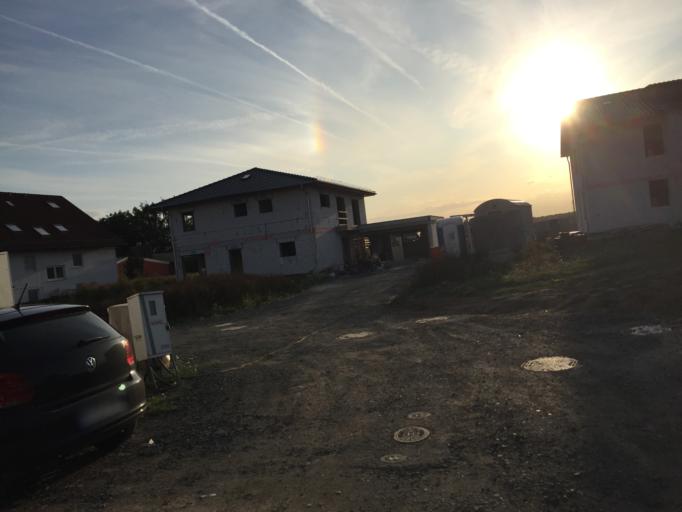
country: DE
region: Hesse
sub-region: Regierungsbezirk Giessen
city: Alten Buseck
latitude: 50.6121
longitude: 8.7548
